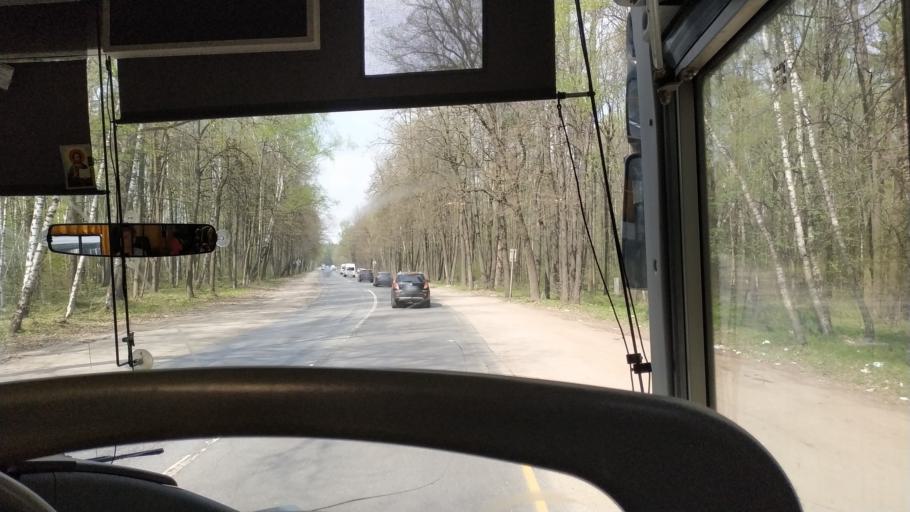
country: RU
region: Moskovskaya
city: Lytkarino
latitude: 55.5928
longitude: 37.9152
